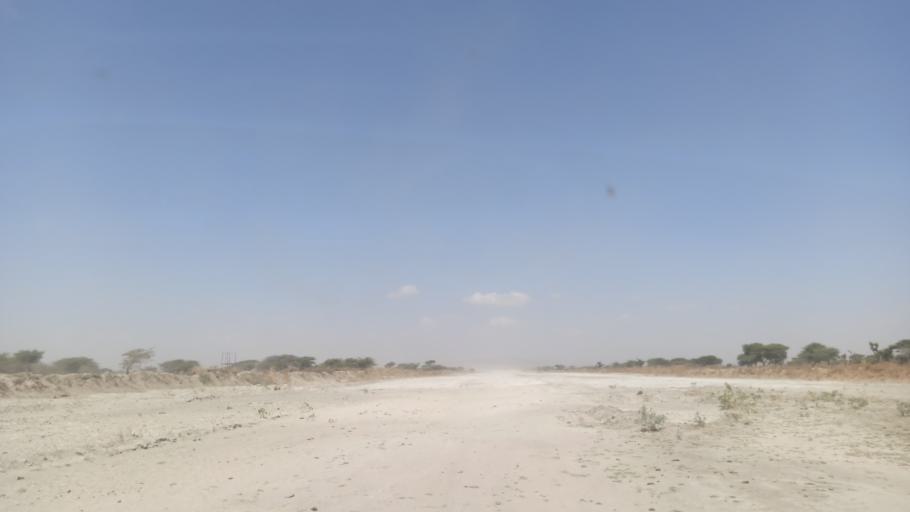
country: ET
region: Oromiya
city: Ziway
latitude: 7.7127
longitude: 38.6350
